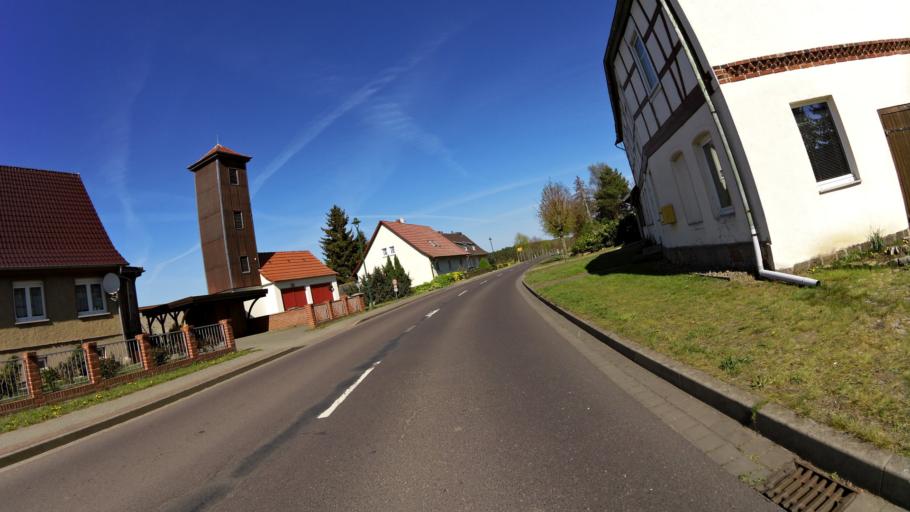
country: DE
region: Saxony-Anhalt
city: Kalbe
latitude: 52.6550
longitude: 11.4662
